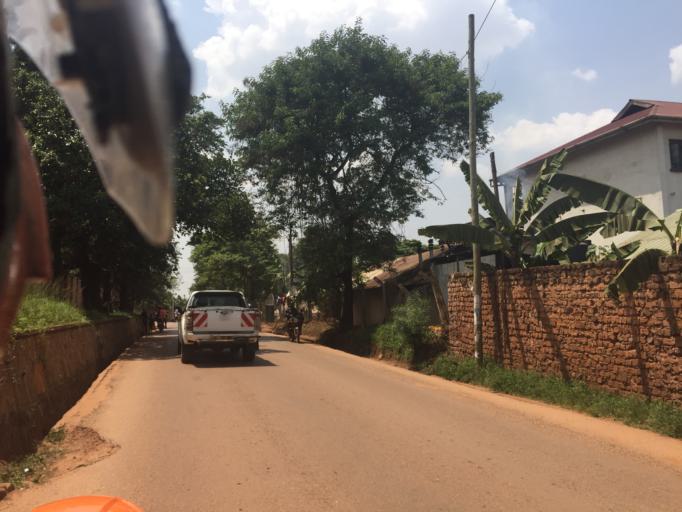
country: UG
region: Central Region
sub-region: Kampala District
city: Kampala
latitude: 0.3008
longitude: 32.5887
